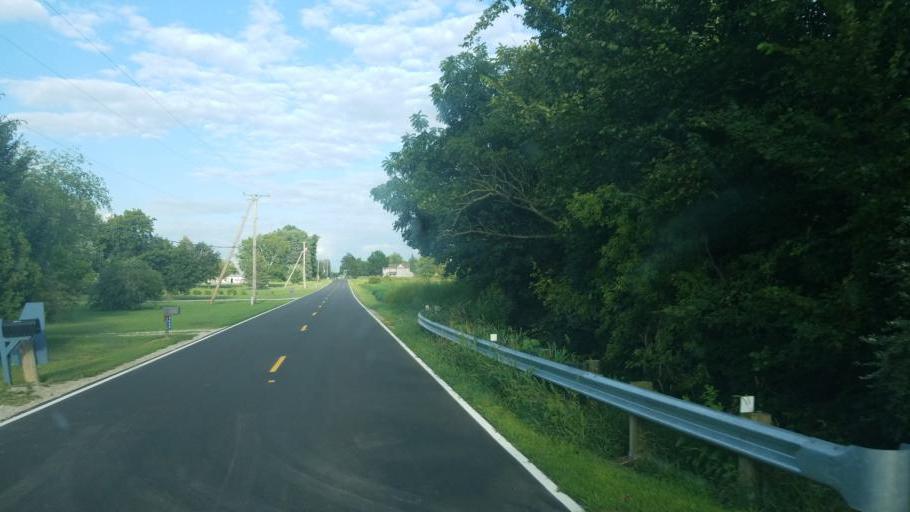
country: US
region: Ohio
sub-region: Seneca County
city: Tiffin
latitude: 41.1097
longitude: -83.1192
